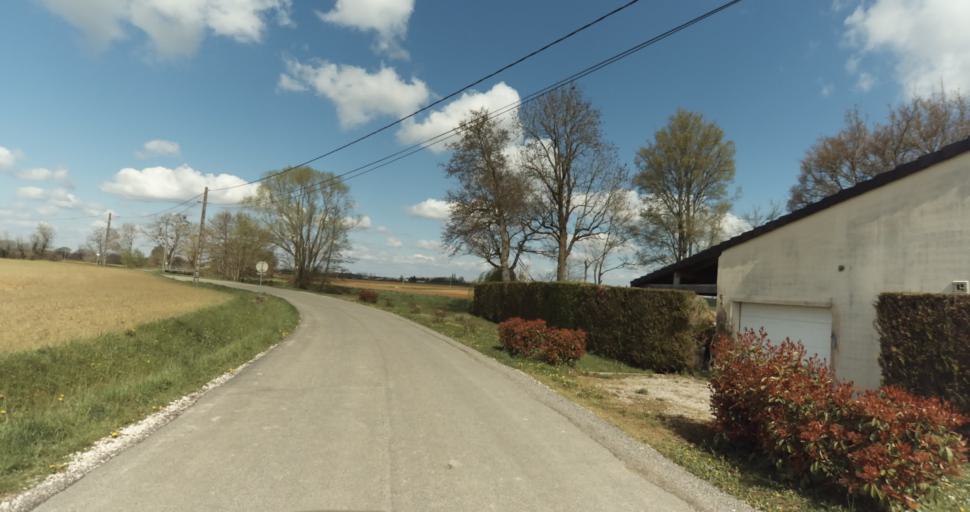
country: FR
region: Bourgogne
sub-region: Departement de la Cote-d'Or
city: Auxonne
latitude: 47.2023
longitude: 5.4250
